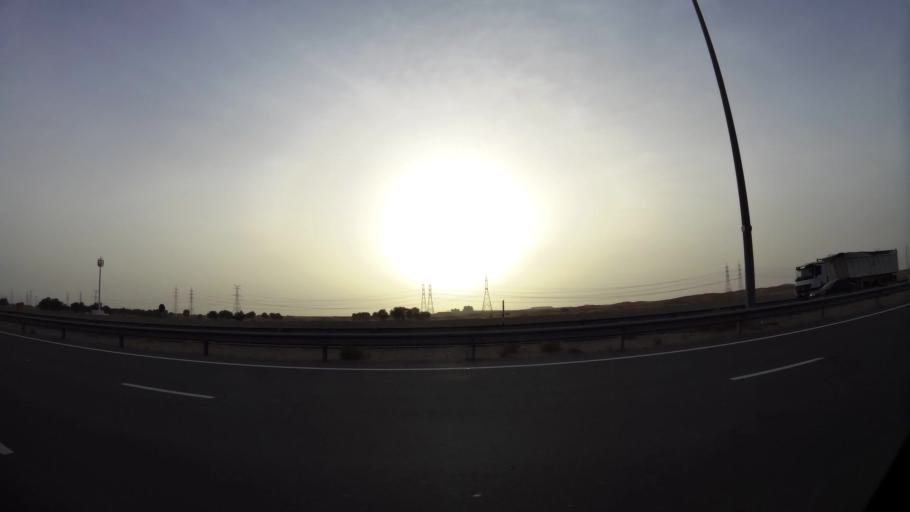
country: OM
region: Al Buraimi
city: Al Buraymi
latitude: 24.2873
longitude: 55.7348
